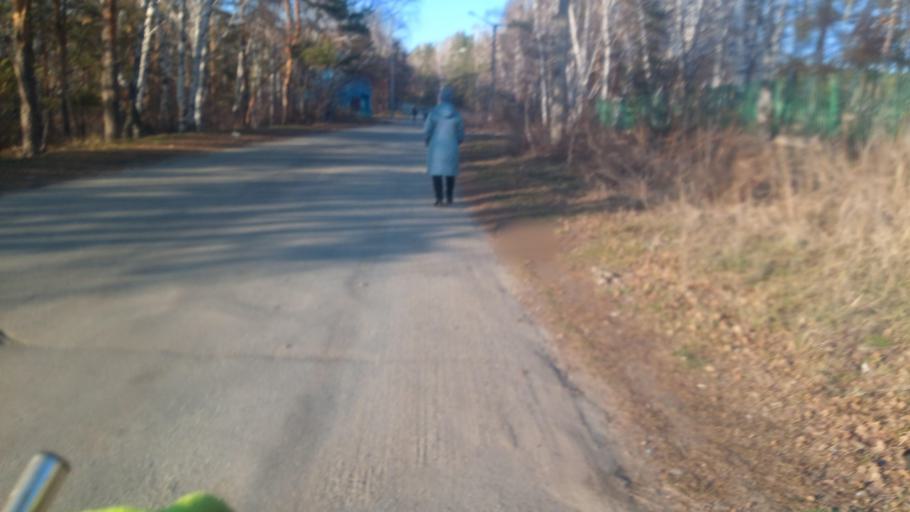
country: RU
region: Chelyabinsk
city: Novosineglazovskiy
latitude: 55.1250
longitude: 61.3297
